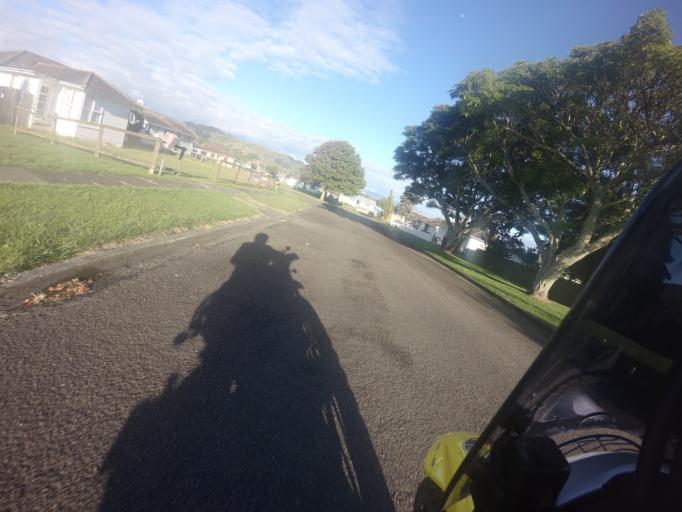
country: NZ
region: Gisborne
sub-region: Gisborne District
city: Gisborne
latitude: -38.6726
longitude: 178.0579
